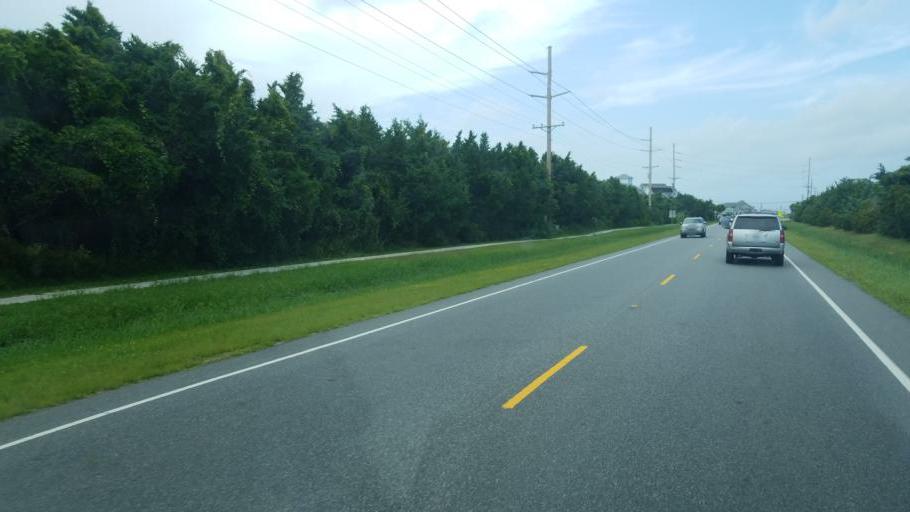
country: US
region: North Carolina
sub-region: Dare County
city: Buxton
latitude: 35.3288
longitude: -75.5078
